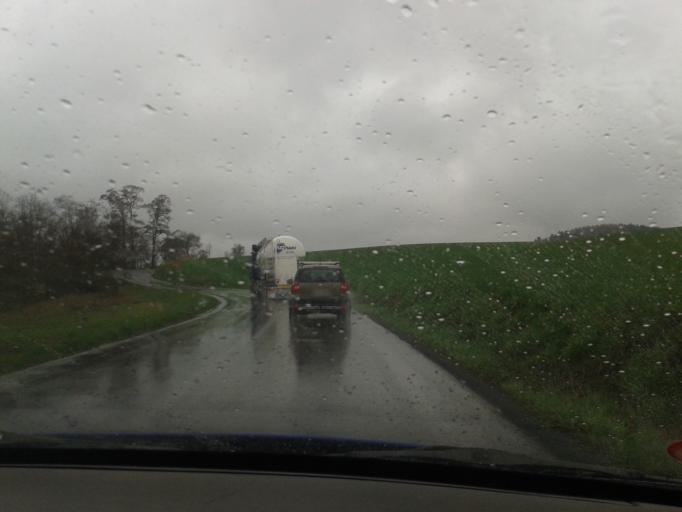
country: CZ
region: Central Bohemia
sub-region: Okres Beroun
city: Kraluv Dvur
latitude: 49.9371
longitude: 14.0407
